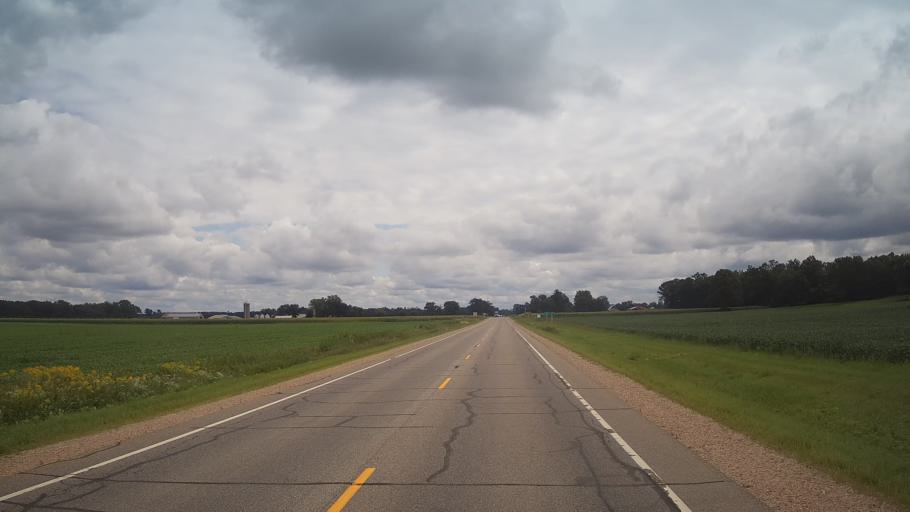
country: US
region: Wisconsin
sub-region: Adams County
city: Friendship
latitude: 44.0393
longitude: -89.9217
